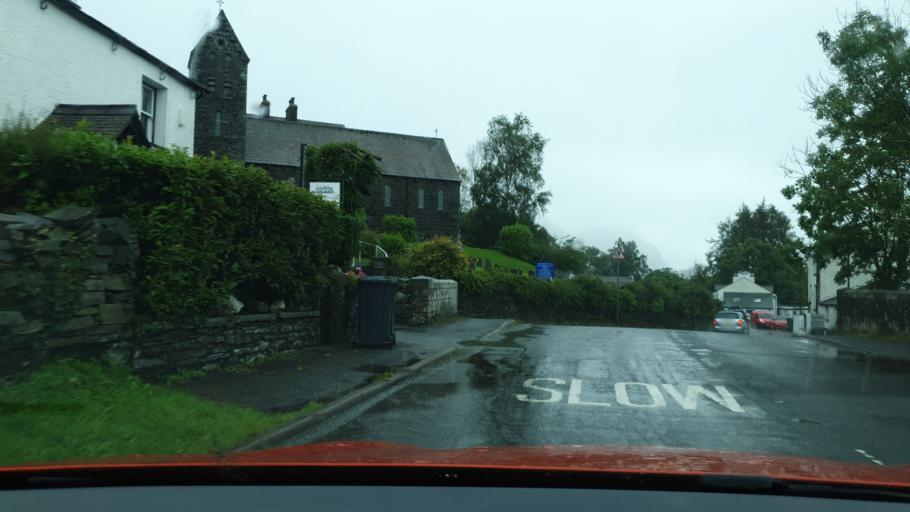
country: GB
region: England
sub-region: Cumbria
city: Ambleside
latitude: 54.3607
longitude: -3.0795
